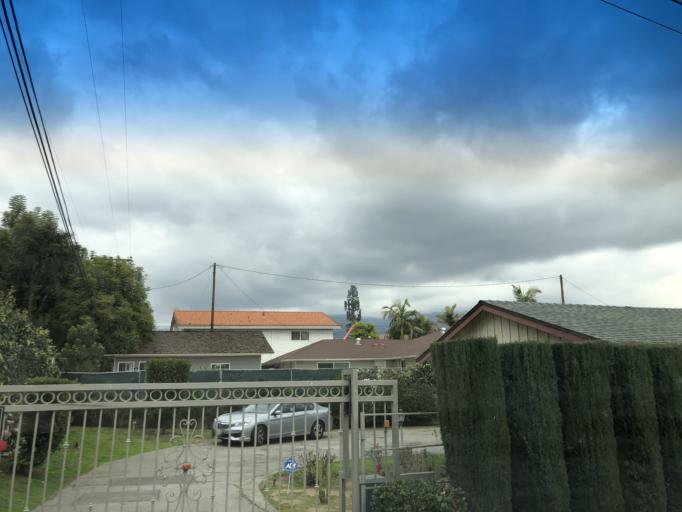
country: US
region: California
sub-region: Los Angeles County
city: San Marino
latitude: 34.1259
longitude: -118.0883
